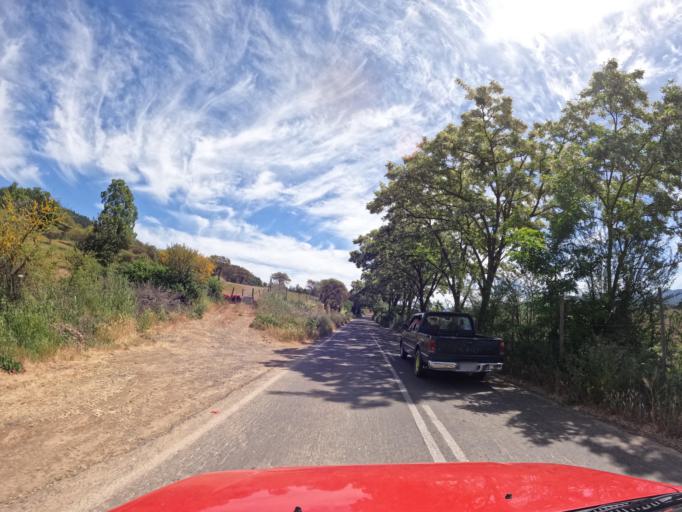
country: CL
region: Maule
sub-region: Provincia de Talca
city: Talca
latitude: -34.9893
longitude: -71.8357
